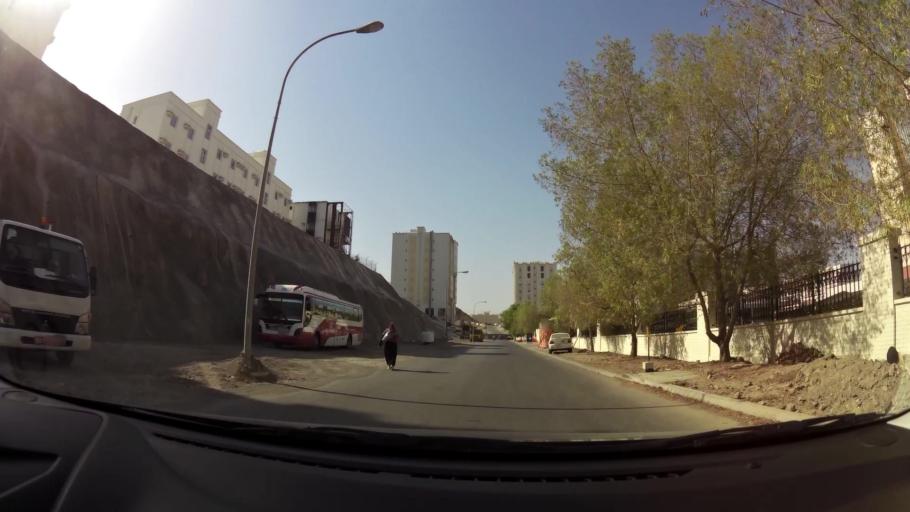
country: OM
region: Muhafazat Masqat
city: Muscat
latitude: 23.5984
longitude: 58.5530
